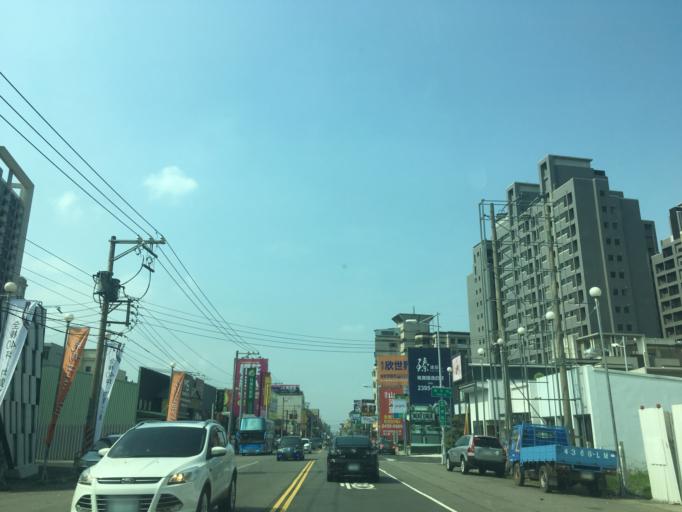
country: TW
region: Taiwan
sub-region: Taichung City
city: Taichung
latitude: 24.1605
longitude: 120.7134
